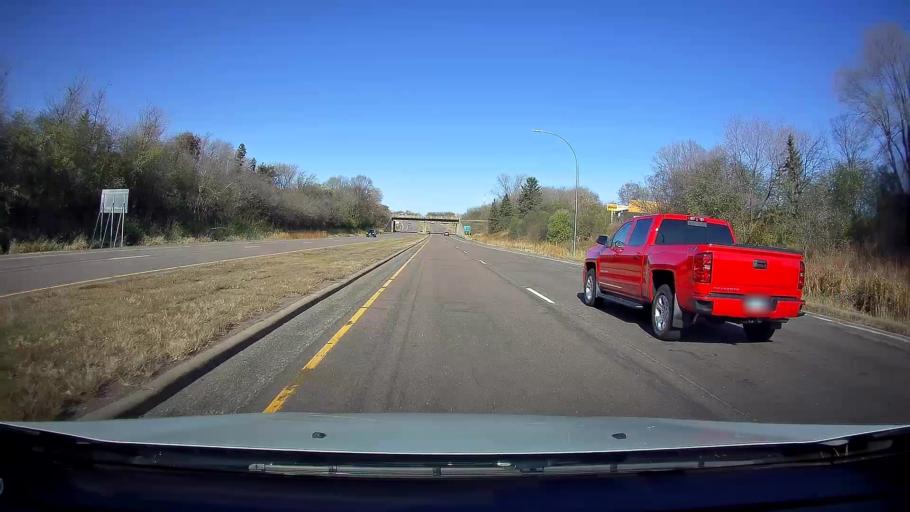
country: US
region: Minnesota
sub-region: Ramsey County
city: Arden Hills
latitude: 45.0507
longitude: -93.1568
